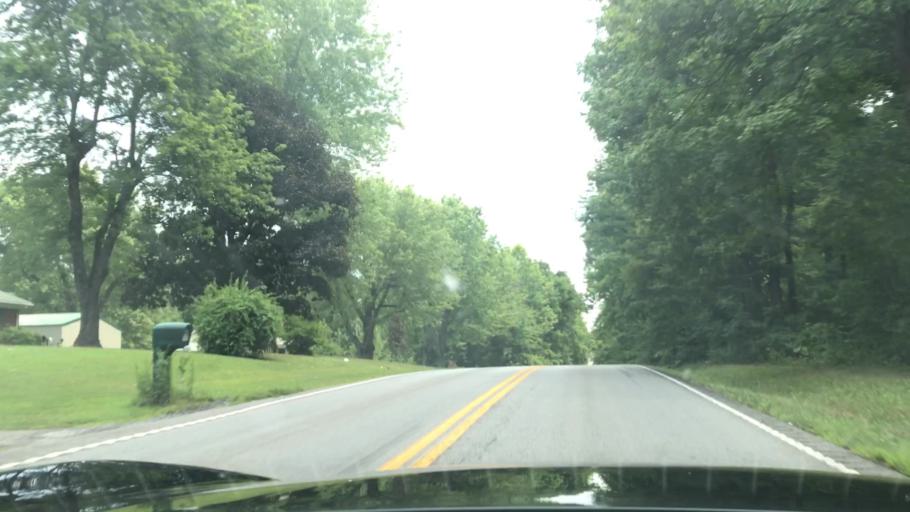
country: US
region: Kentucky
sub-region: Muhlenberg County
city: Greenville
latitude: 37.2030
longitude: -87.0934
